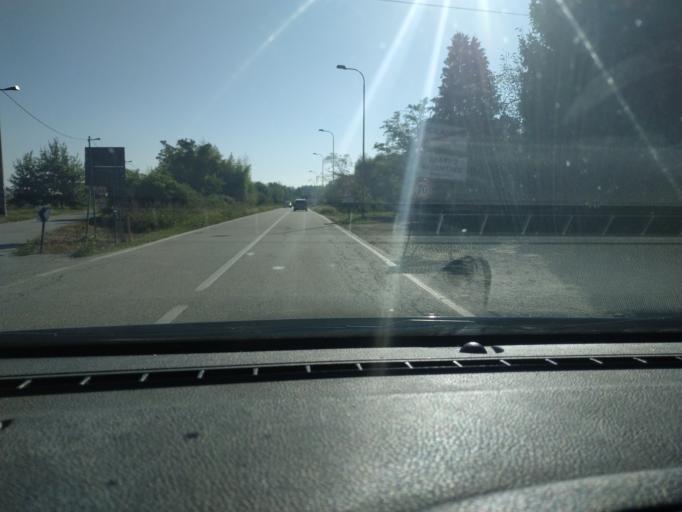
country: IT
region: Piedmont
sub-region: Provincia di Torino
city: Verolengo
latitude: 45.1952
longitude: 7.9458
